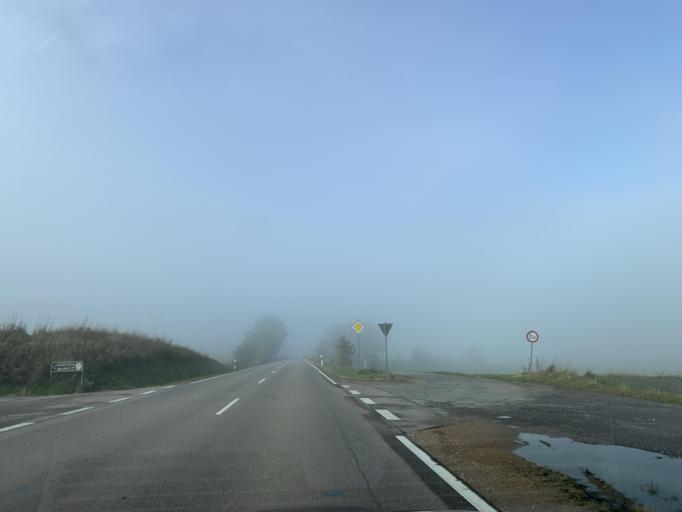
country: DE
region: Bavaria
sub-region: Upper Palatinate
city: Brunn
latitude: 49.2396
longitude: 12.1922
